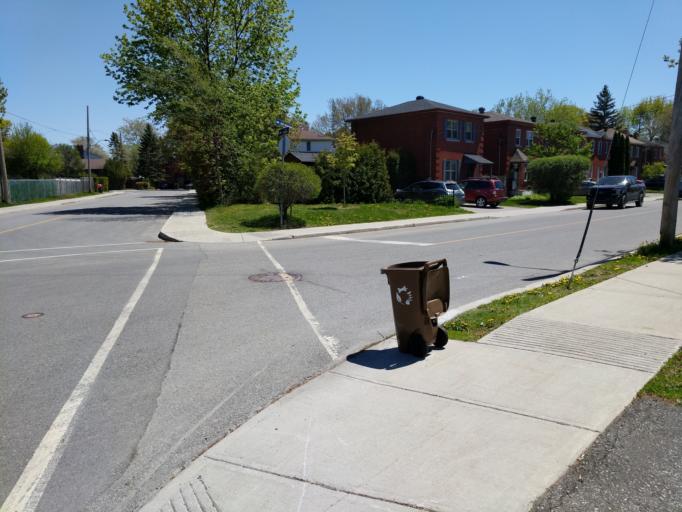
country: CA
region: Quebec
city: Dorval
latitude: 45.4433
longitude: -73.7170
